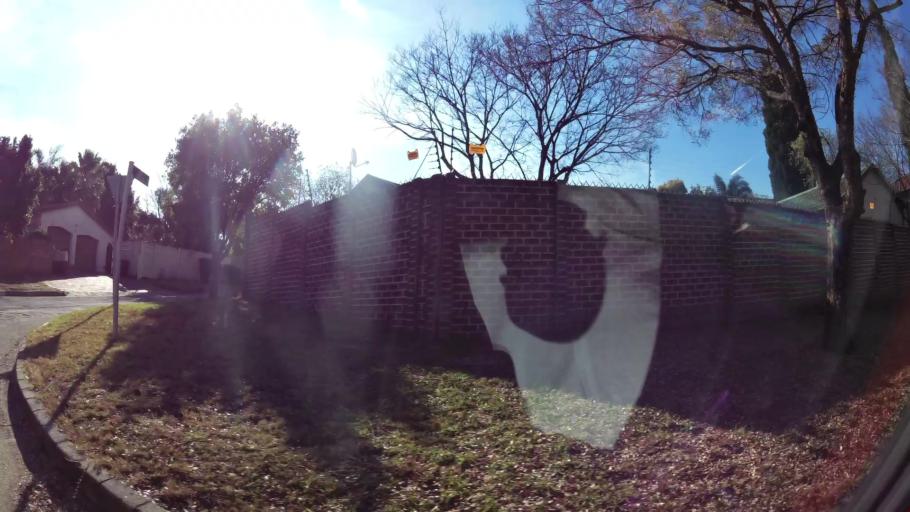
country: ZA
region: Gauteng
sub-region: City of Johannesburg Metropolitan Municipality
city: Roodepoort
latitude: -26.1018
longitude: 27.9544
